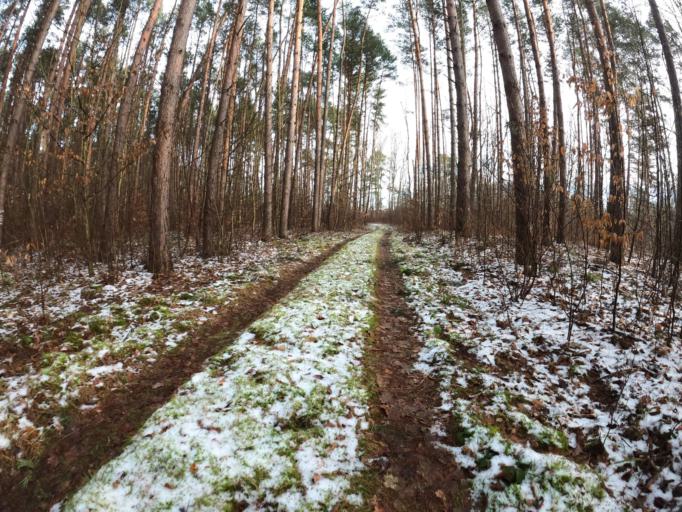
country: PL
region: Lubusz
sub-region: Powiat slubicki
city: Rzepin
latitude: 52.3130
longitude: 14.8263
